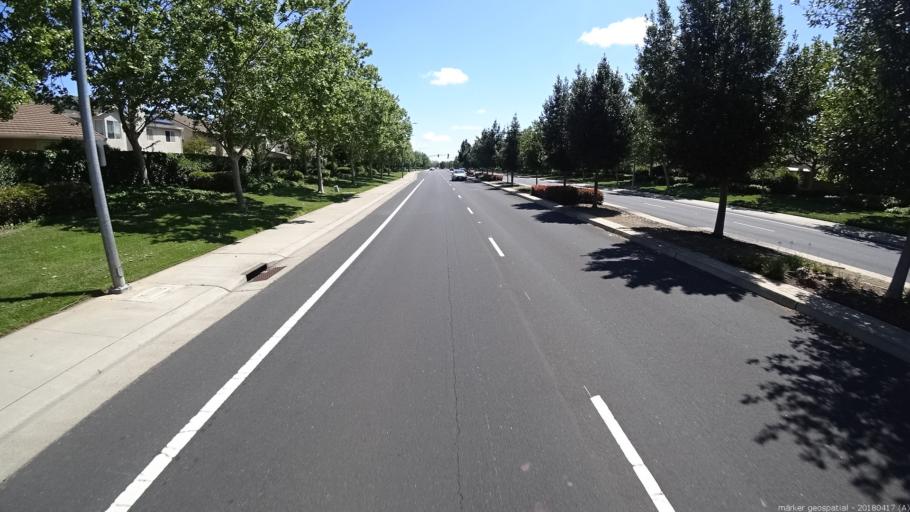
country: US
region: California
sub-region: Sacramento County
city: Laguna
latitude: 38.4191
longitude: -121.4812
